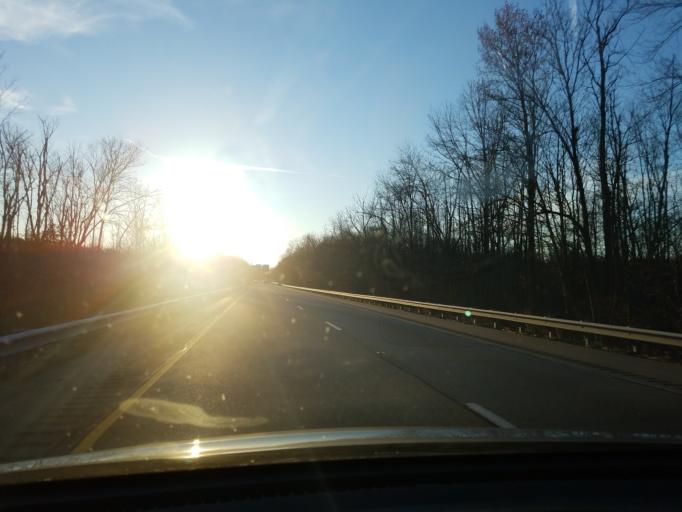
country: US
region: Indiana
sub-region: Warrick County
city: Chandler
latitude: 38.1734
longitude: -87.4219
